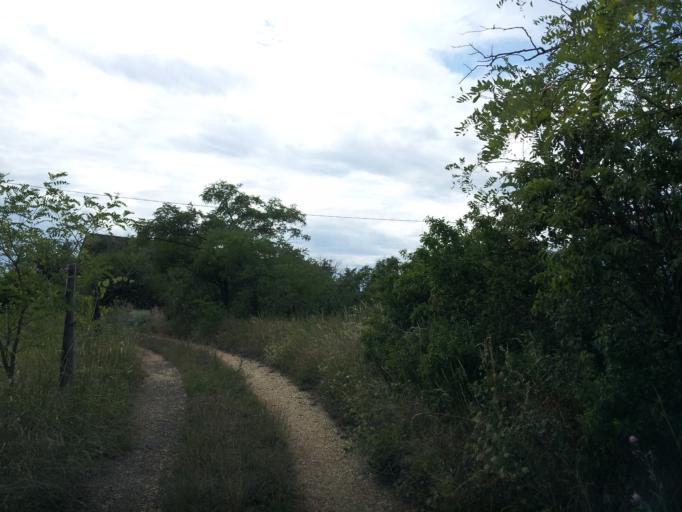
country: HU
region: Vas
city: Janoshaza
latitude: 47.1495
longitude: 17.1004
